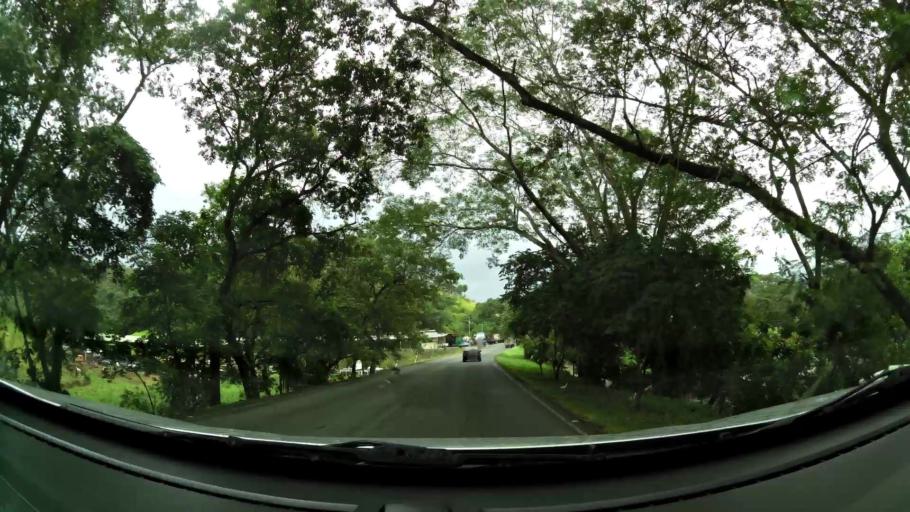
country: CR
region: Puntarenas
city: Esparza
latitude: 9.9962
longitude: -84.6985
